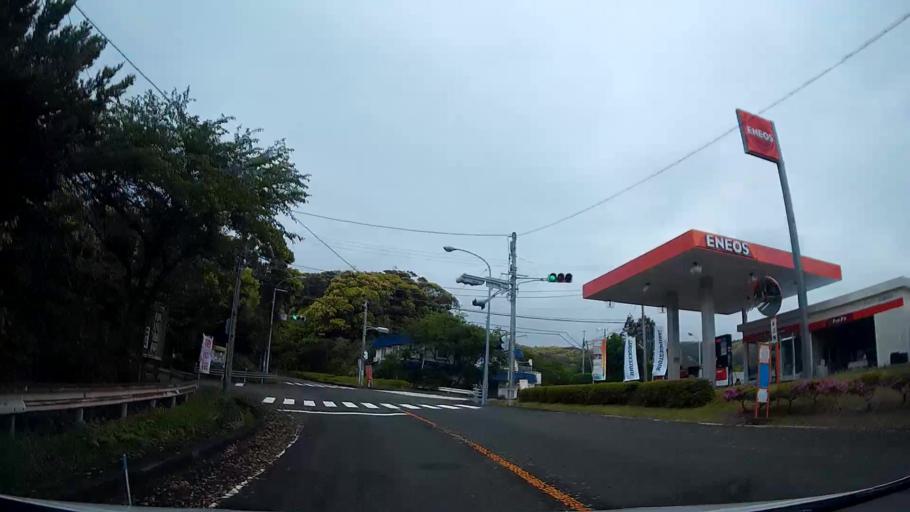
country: JP
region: Shizuoka
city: Shimoda
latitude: 34.6842
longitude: 138.7786
